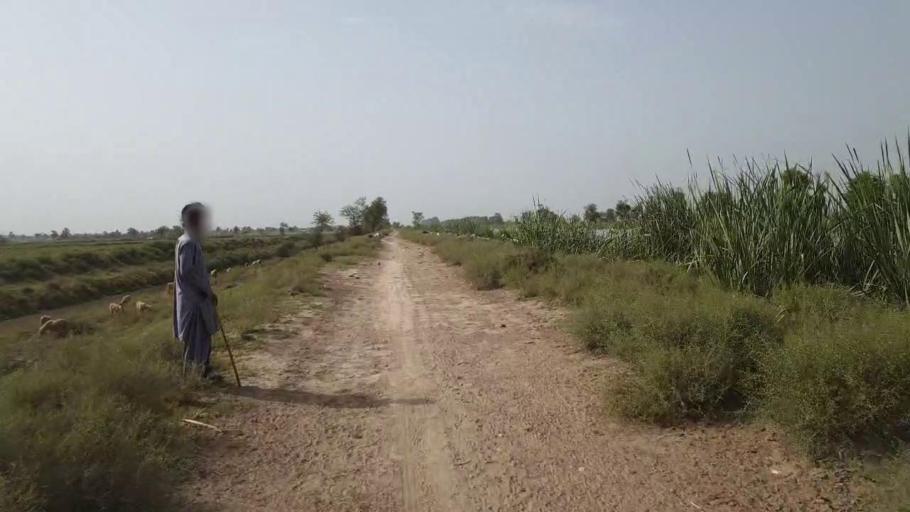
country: PK
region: Sindh
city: Daur
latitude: 26.4394
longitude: 68.1618
